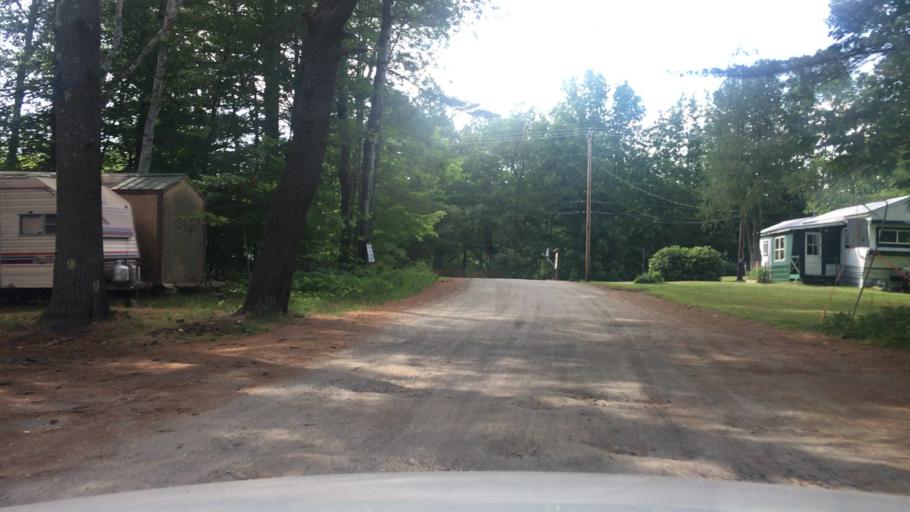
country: US
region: Maine
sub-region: Franklin County
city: Wilton
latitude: 44.5968
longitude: -70.2187
